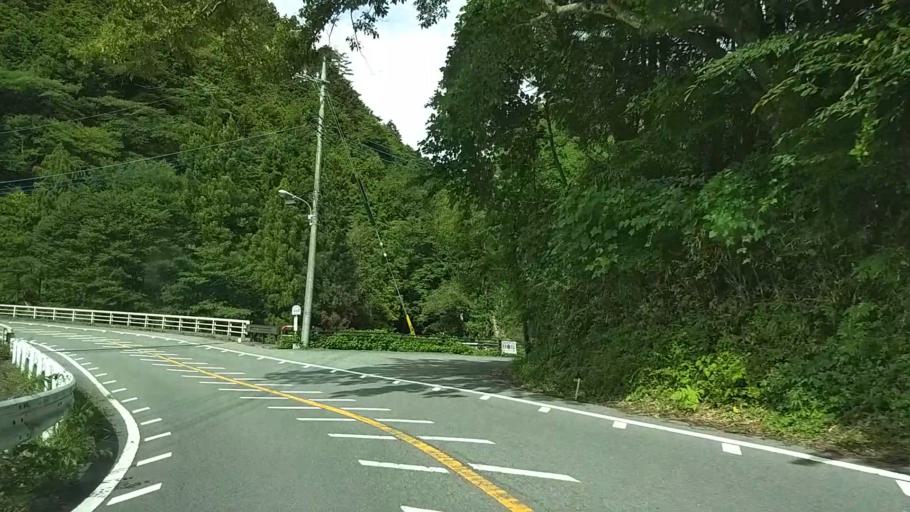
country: JP
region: Yamanashi
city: Uenohara
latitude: 35.5366
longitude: 139.1081
